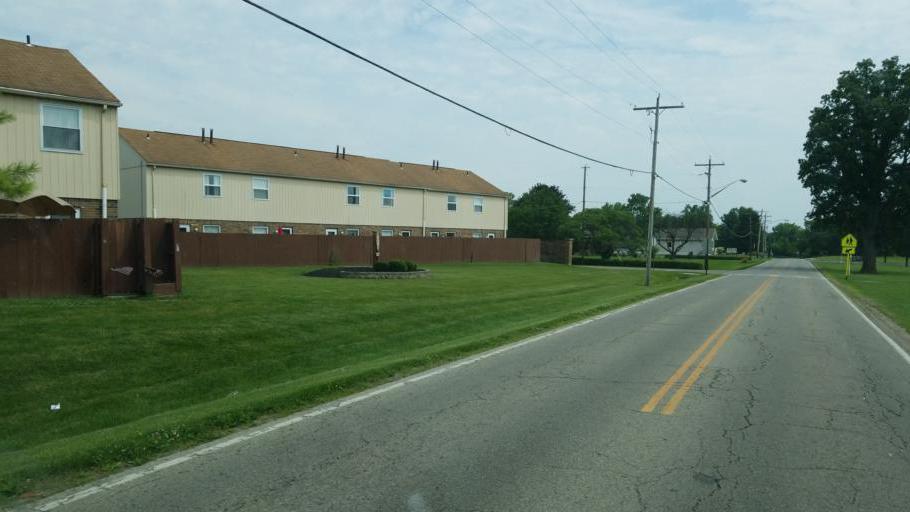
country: US
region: Ohio
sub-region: Madison County
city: West Jefferson
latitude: 39.9344
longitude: -83.2783
